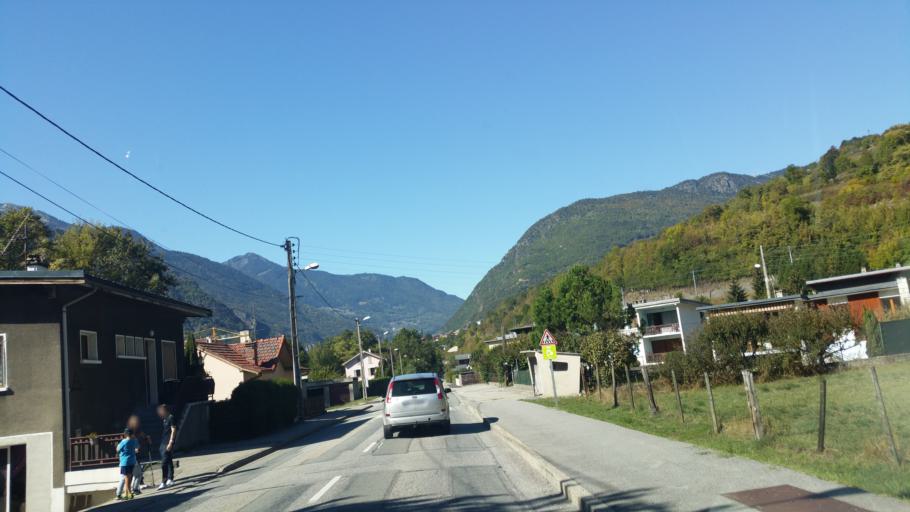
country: FR
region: Rhone-Alpes
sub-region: Departement de la Savoie
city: Aigueblanche
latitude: 45.5060
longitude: 6.5045
